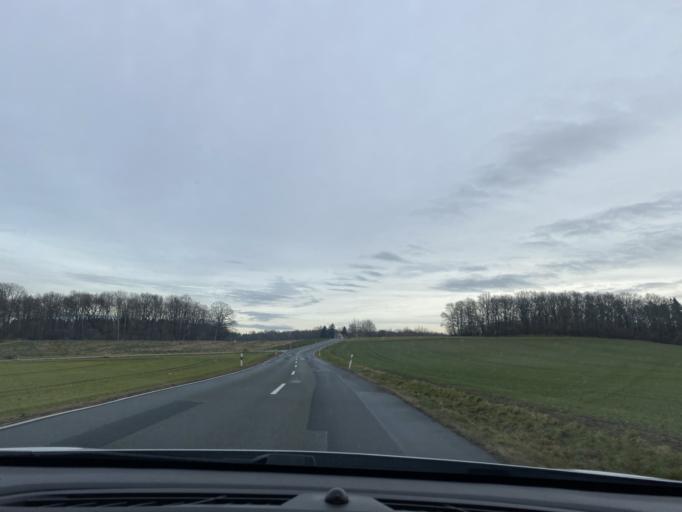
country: DE
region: Saxony
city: Reichenbach
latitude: 51.1291
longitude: 14.8079
